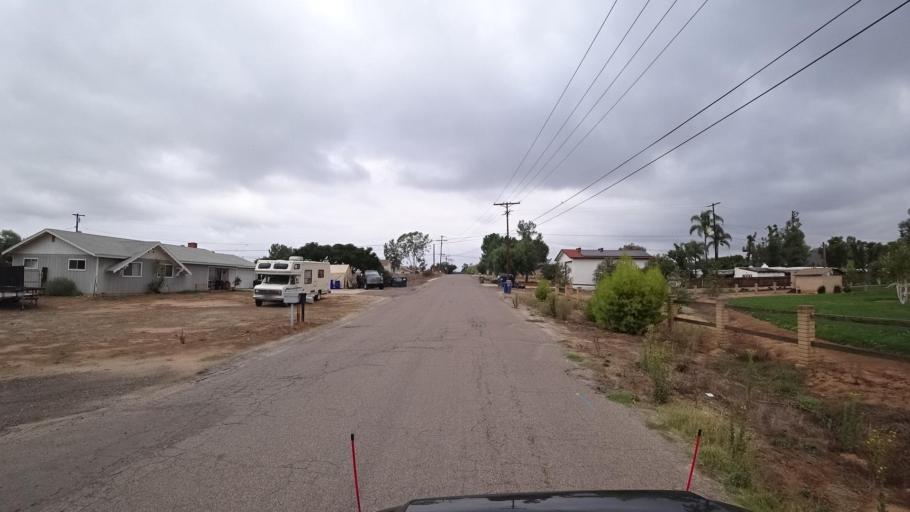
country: US
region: California
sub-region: San Diego County
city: Ramona
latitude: 33.0243
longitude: -116.8578
